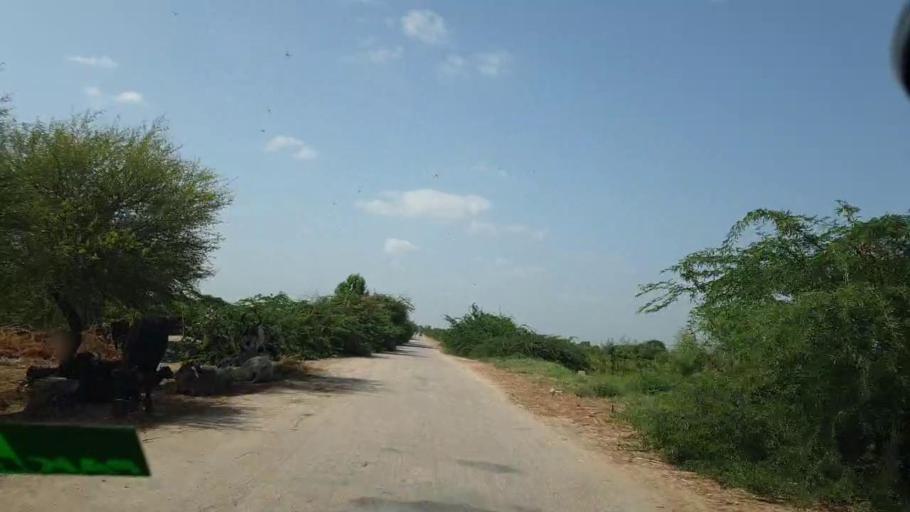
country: PK
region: Sindh
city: Tando Bago
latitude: 24.6771
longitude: 69.1917
